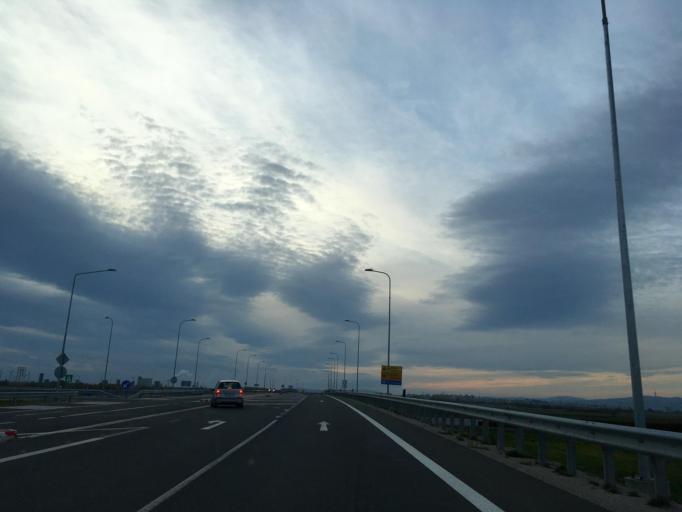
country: SK
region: Bratislavsky
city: Dunajska Luzna
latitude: 48.1320
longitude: 17.2533
